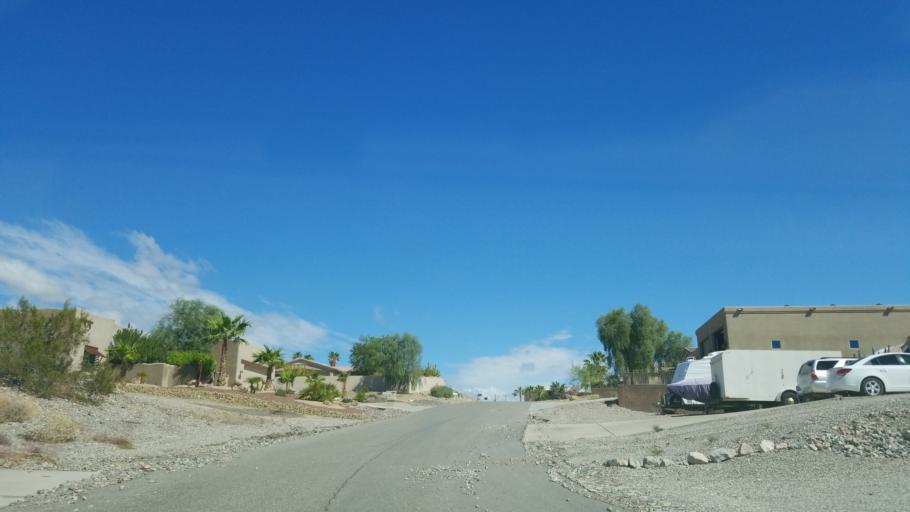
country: US
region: Arizona
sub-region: Mohave County
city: Lake Havasu City
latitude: 34.4663
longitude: -114.2574
